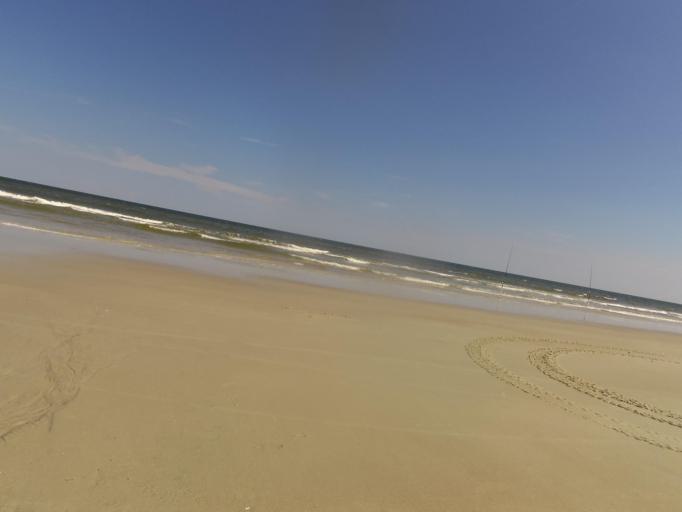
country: US
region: Florida
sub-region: Nassau County
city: Fernandina Beach
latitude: 30.6453
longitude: -81.4337
